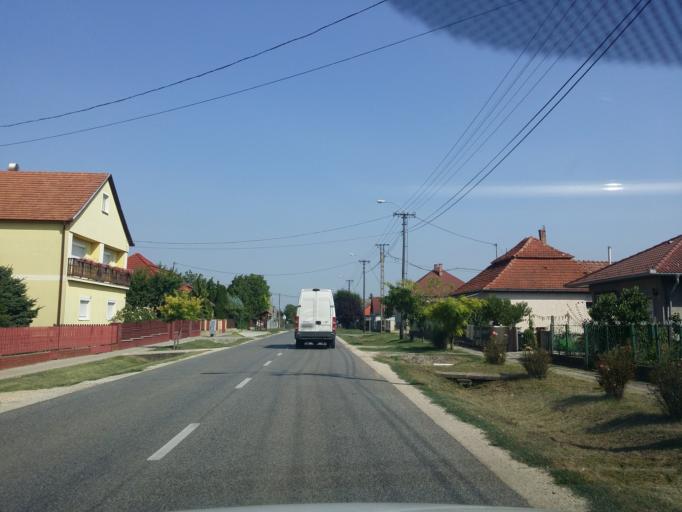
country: HU
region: Fejer
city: Mezofalva
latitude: 46.9325
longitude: 18.7696
